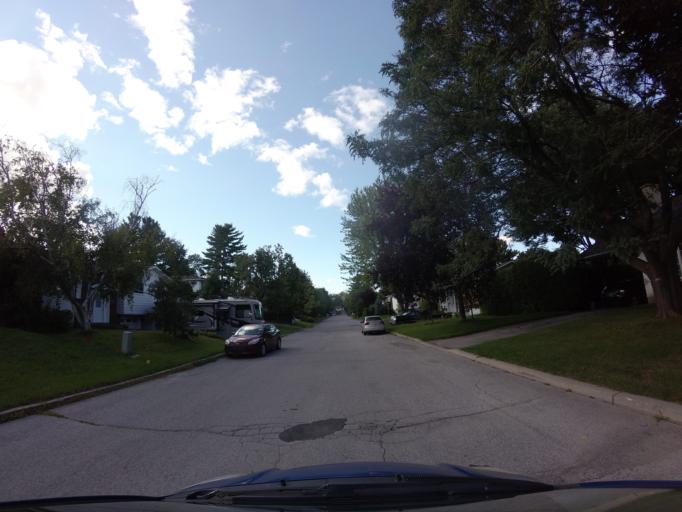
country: CA
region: Quebec
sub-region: Outaouais
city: Gatineau
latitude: 45.4881
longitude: -75.7320
